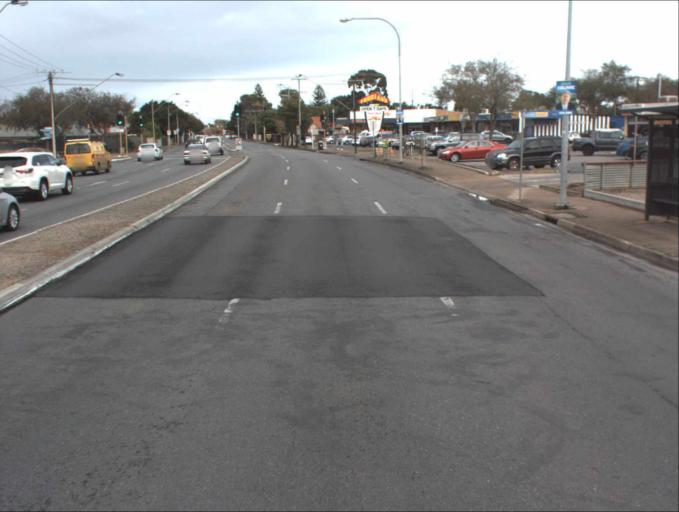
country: AU
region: South Australia
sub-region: Prospect
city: Prospect
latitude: -34.8897
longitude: 138.6127
